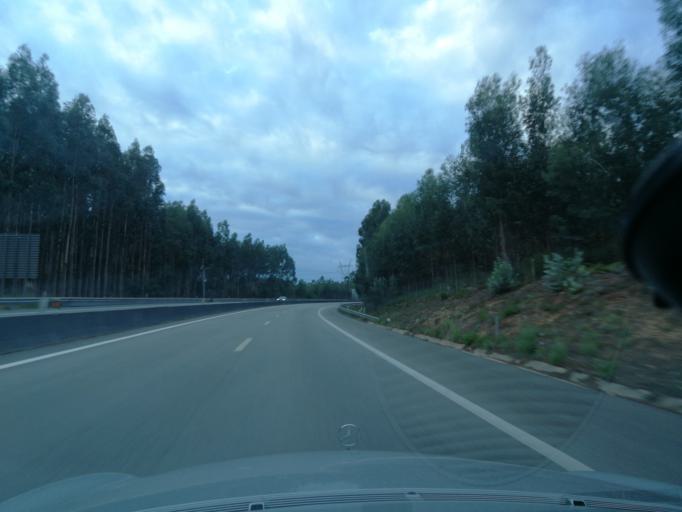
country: PT
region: Aveiro
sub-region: Albergaria-A-Velha
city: Albergaria-a-Velha
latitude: 40.6816
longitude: -8.4946
